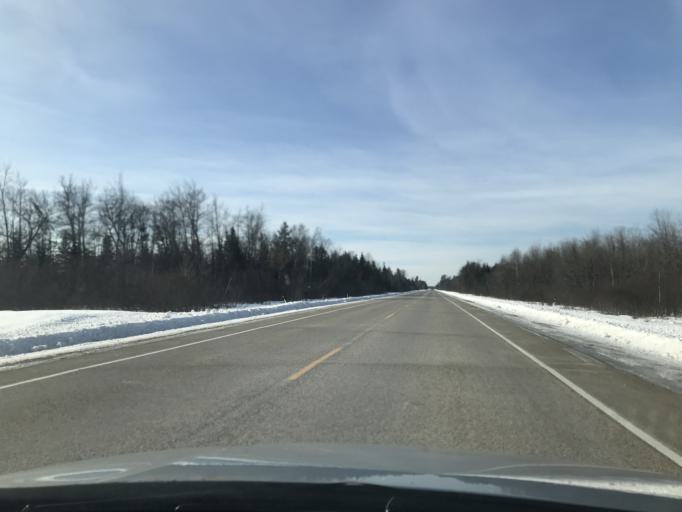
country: US
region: Wisconsin
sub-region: Oconto County
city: Gillett
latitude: 45.1142
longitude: -88.3310
